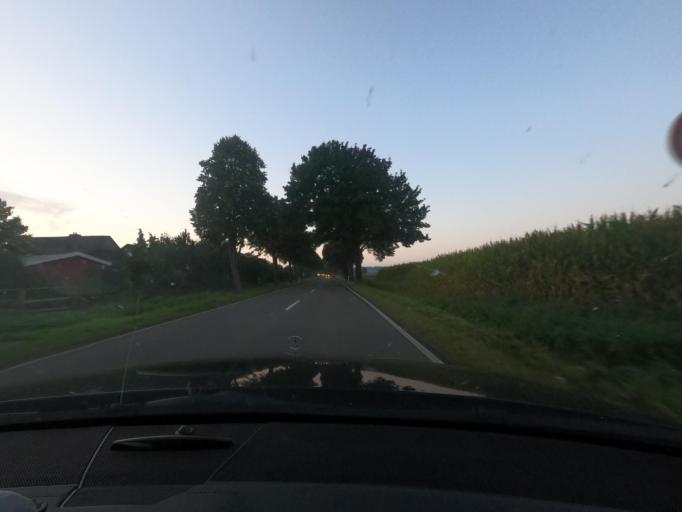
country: DE
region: North Rhine-Westphalia
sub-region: Regierungsbezirk Detmold
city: Salzkotten
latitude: 51.6612
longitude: 8.5907
